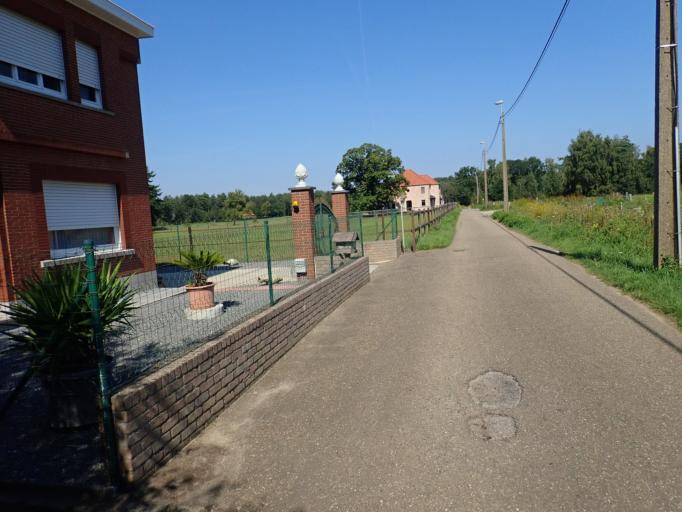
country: BE
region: Flanders
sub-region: Provincie Vlaams-Brabant
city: Scherpenheuvel-Zichem
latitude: 51.0282
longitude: 4.9543
